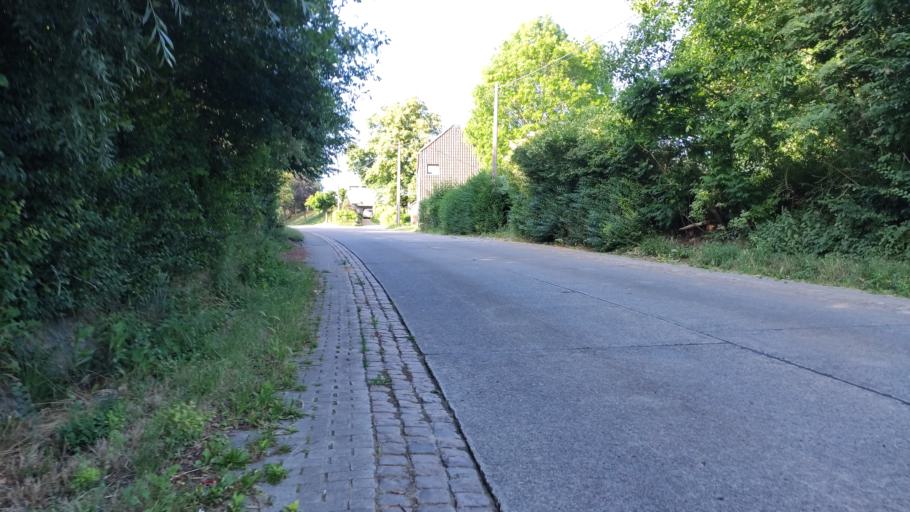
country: BE
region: Flanders
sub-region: Provincie Vlaams-Brabant
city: Hoegaarden
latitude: 50.7666
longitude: 4.8872
